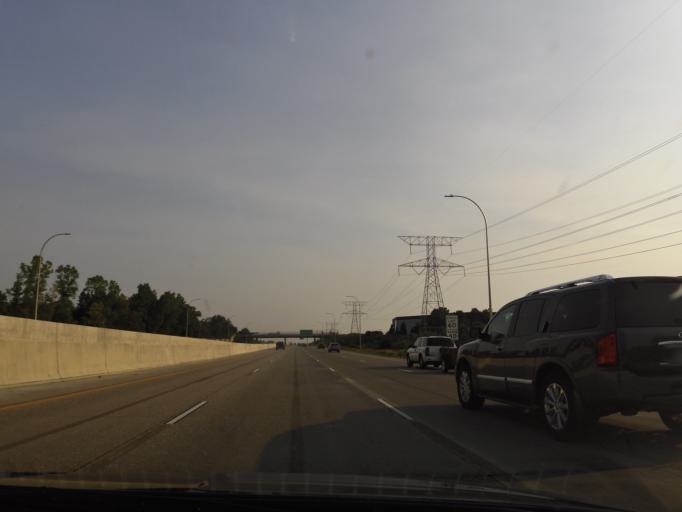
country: US
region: Minnesota
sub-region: Hennepin County
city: Maple Grove
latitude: 45.0840
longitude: -93.4471
